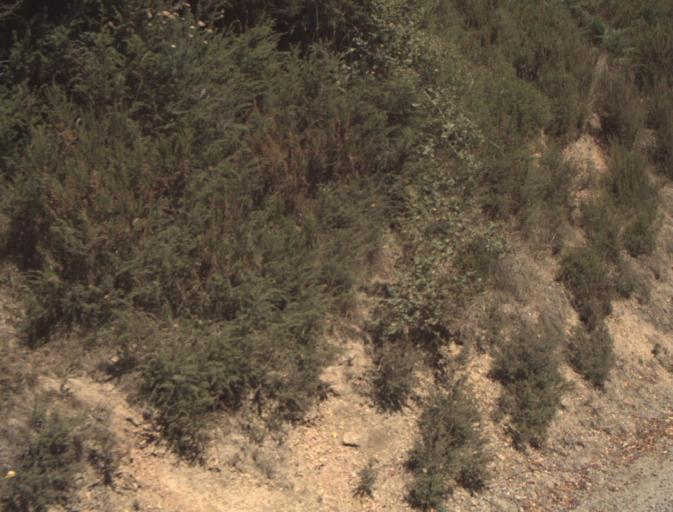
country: AU
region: Tasmania
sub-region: Dorset
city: Scottsdale
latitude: -41.2944
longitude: 147.4027
